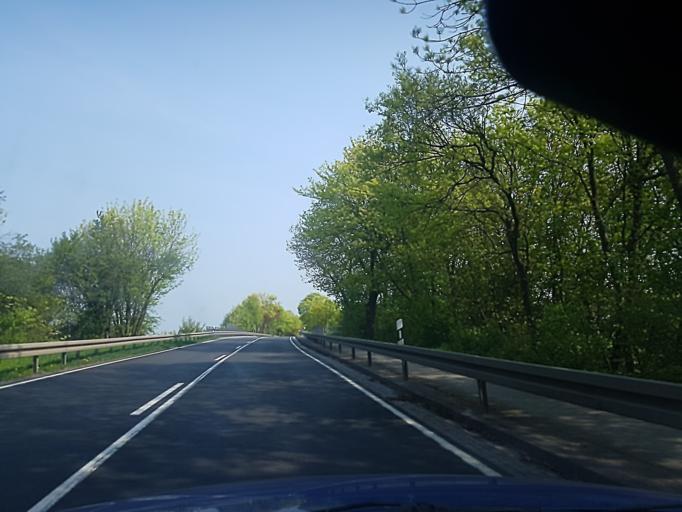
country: DE
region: Saxony
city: Torgau
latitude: 51.5673
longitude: 13.0235
